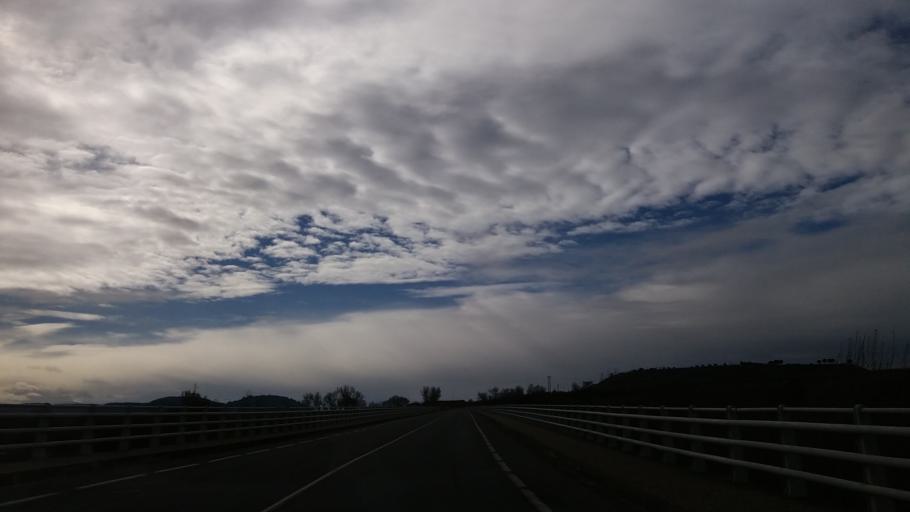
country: ES
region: La Rioja
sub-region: Provincia de La Rioja
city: San Vicente de la Sonsierra
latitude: 42.5584
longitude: -2.7599
